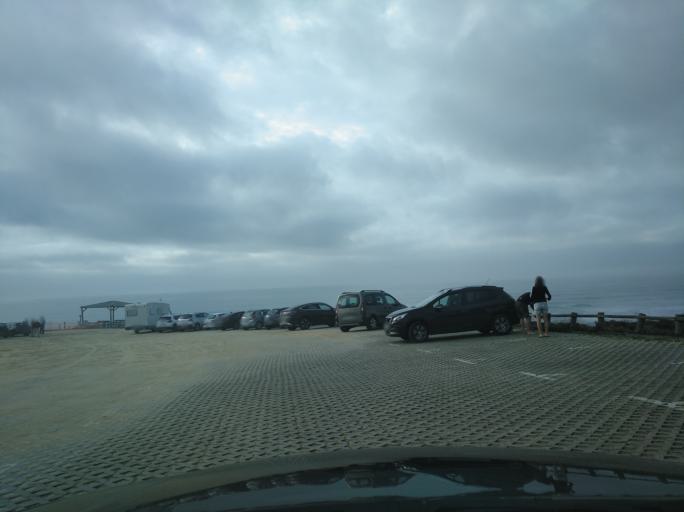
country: PT
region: Beja
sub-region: Odemira
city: Vila Nova de Milfontes
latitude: 37.6534
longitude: -8.8010
